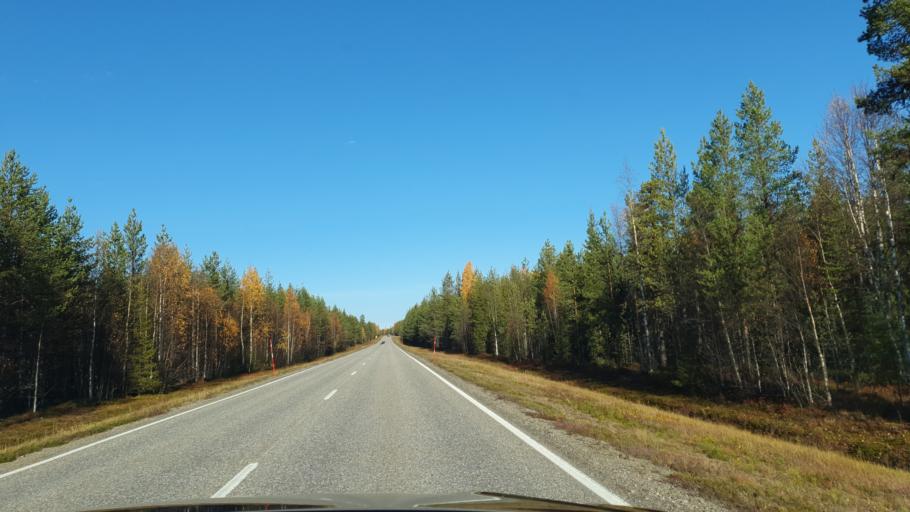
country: FI
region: Lapland
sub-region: Tunturi-Lappi
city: Kittilae
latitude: 67.2389
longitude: 24.9182
